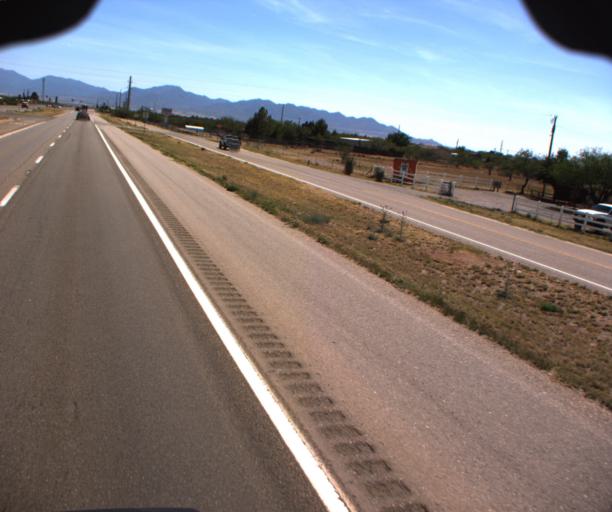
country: US
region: Arizona
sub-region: Cochise County
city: Huachuca City
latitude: 31.6966
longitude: -110.3504
